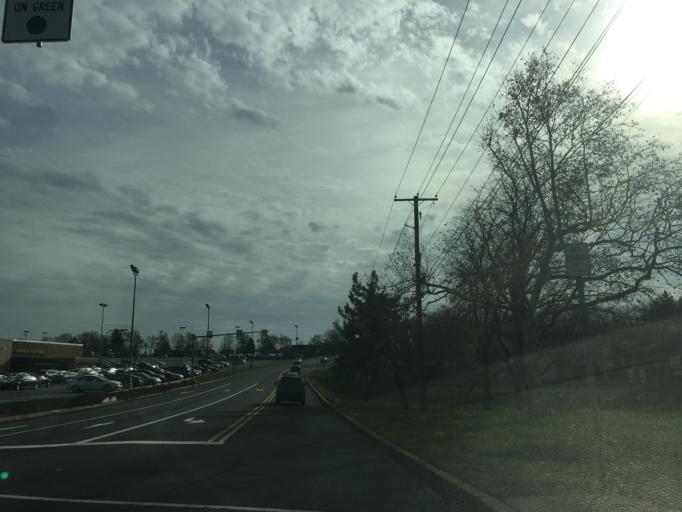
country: US
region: Pennsylvania
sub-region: Dauphin County
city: Colonial Park
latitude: 40.3022
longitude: -76.8218
